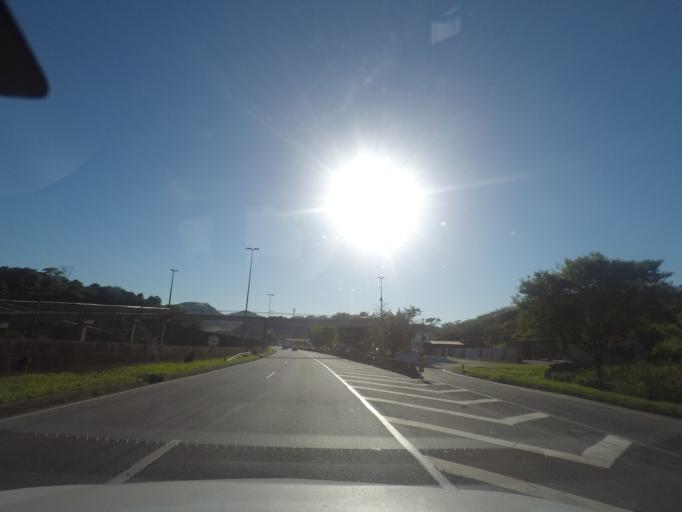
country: BR
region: Rio de Janeiro
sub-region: Petropolis
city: Petropolis
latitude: -22.6576
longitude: -43.1327
